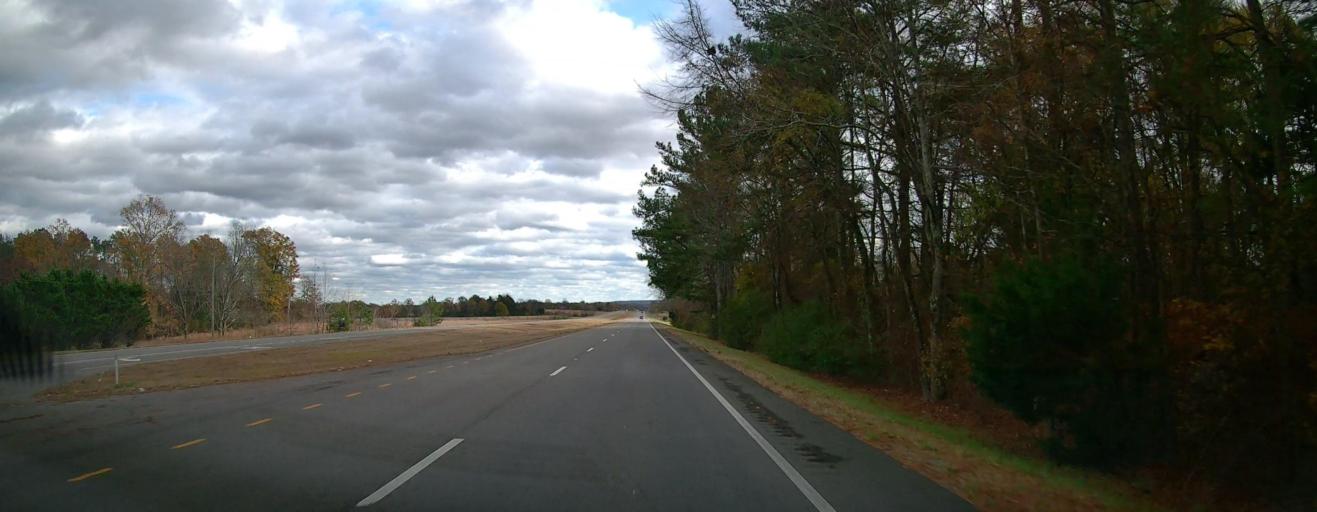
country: US
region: Alabama
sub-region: Morgan County
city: Danville
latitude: 34.3856
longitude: -87.1048
